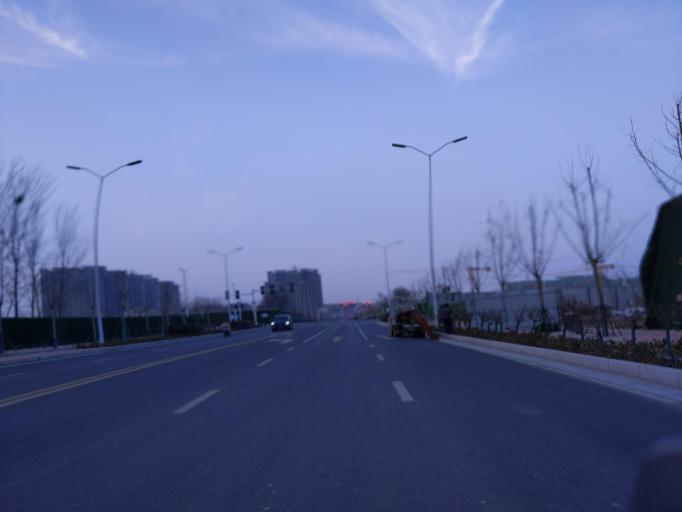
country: CN
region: Henan Sheng
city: Puyang
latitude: 35.8092
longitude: 115.0114
